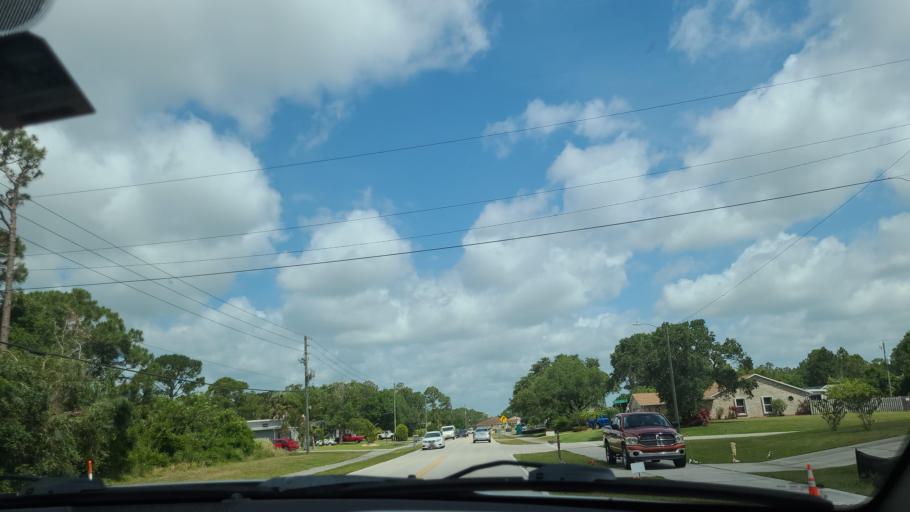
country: US
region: Florida
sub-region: Brevard County
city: June Park
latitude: 27.9926
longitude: -80.6952
